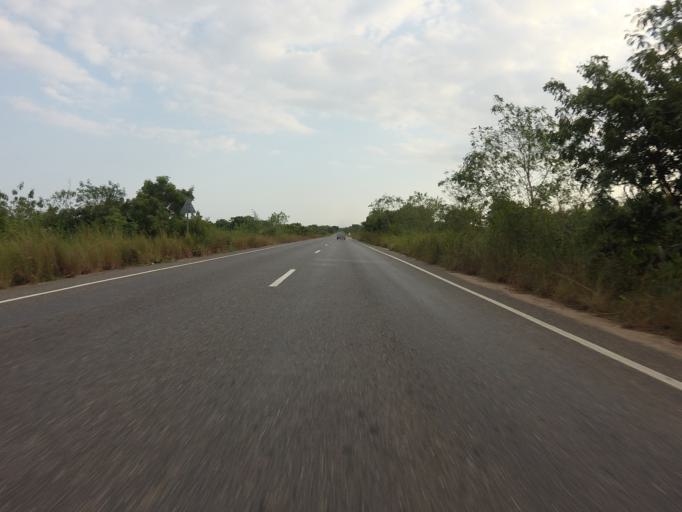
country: GH
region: Volta
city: Ho
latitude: 6.1292
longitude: 0.5233
